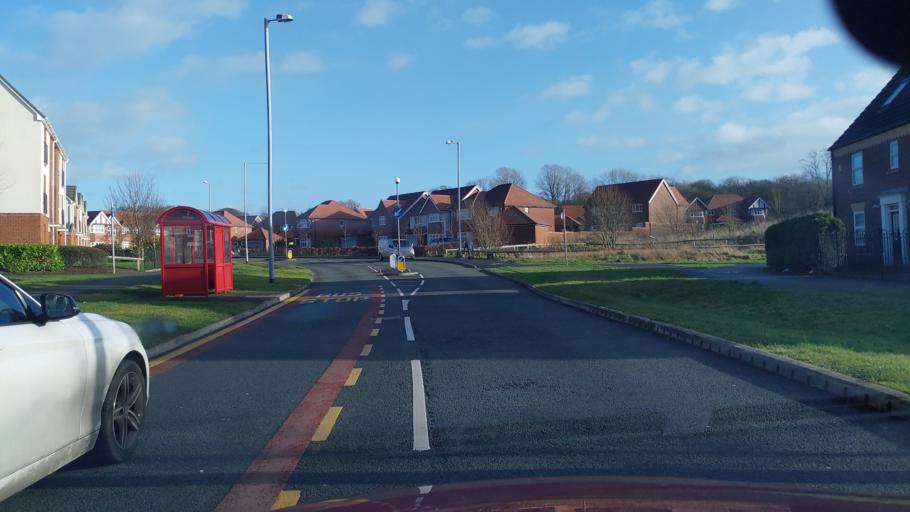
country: GB
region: England
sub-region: Lancashire
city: Clayton-le-Woods
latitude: 53.6798
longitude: -2.6530
